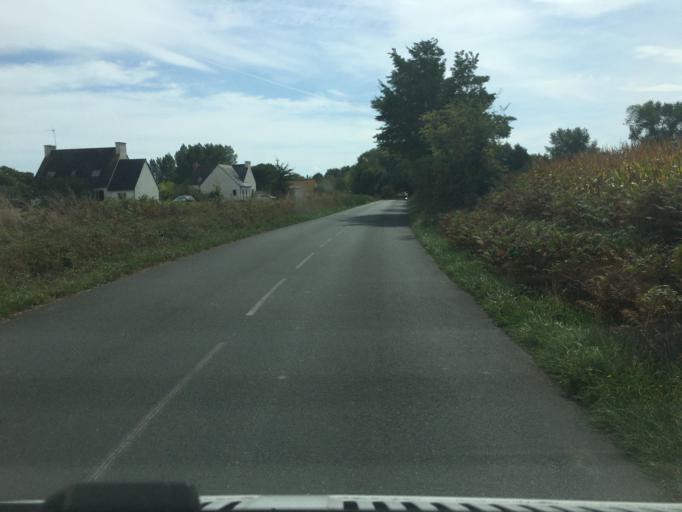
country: FR
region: Brittany
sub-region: Departement du Finistere
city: Loctudy
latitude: 47.8239
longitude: -4.1748
